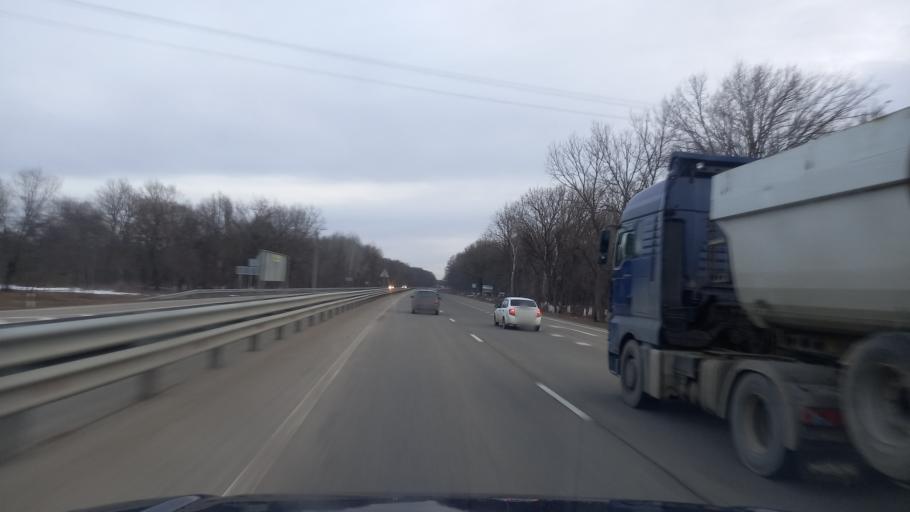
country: RU
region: Krasnodarskiy
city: Yuzhnyy
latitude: 44.7367
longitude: 39.9392
